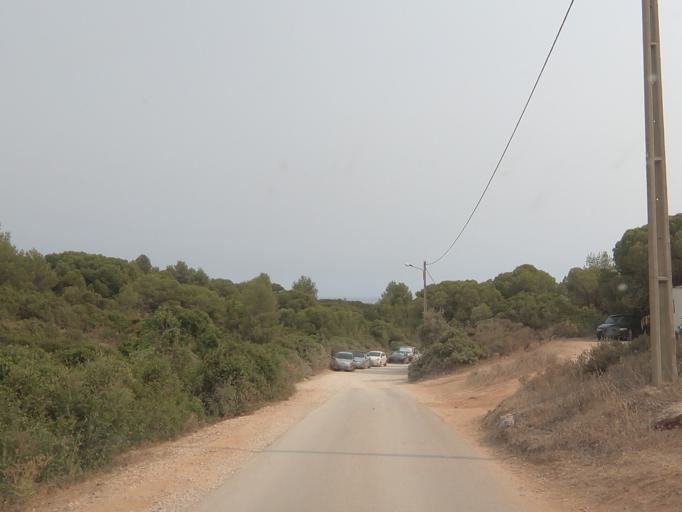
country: PT
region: Faro
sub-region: Silves
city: Armacao de Pera
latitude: 37.0930
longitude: -8.4006
